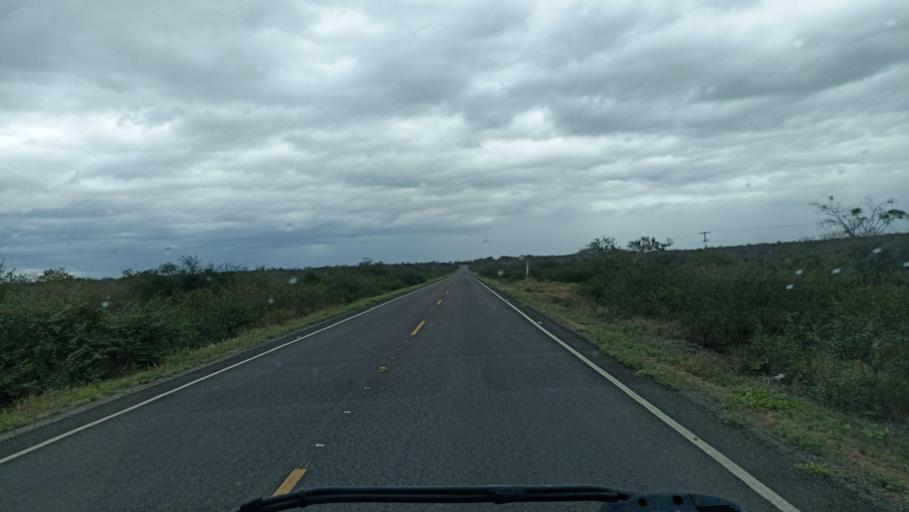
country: BR
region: Bahia
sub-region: Iacu
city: Iacu
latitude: -12.9741
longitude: -40.5079
